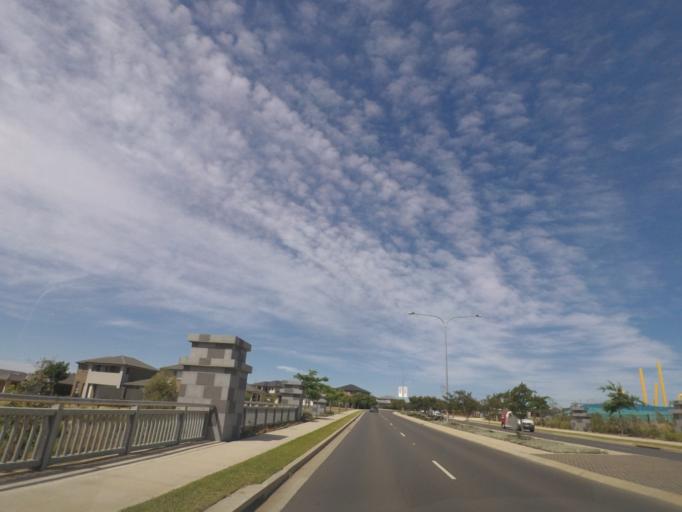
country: AU
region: New South Wales
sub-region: Camden
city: Narellan Vale
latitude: -34.0249
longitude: 150.7785
